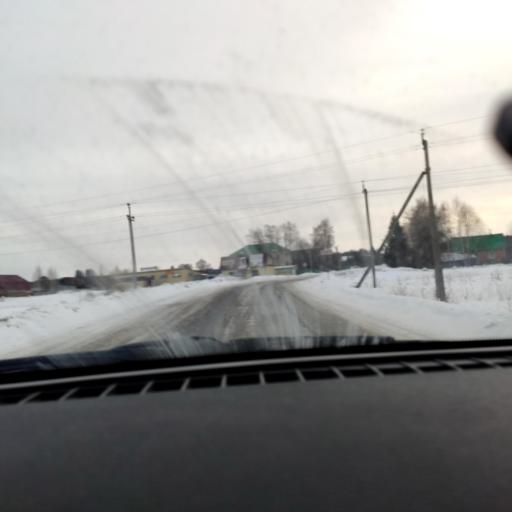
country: RU
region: Bashkortostan
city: Iglino
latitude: 54.7771
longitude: 56.5379
